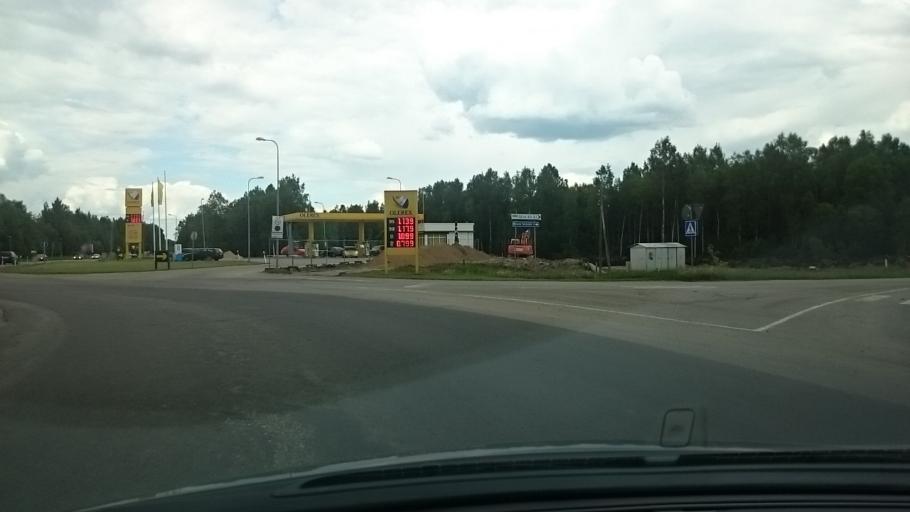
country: EE
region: Jaervamaa
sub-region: Paide linn
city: Paide
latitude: 58.8940
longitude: 25.5702
